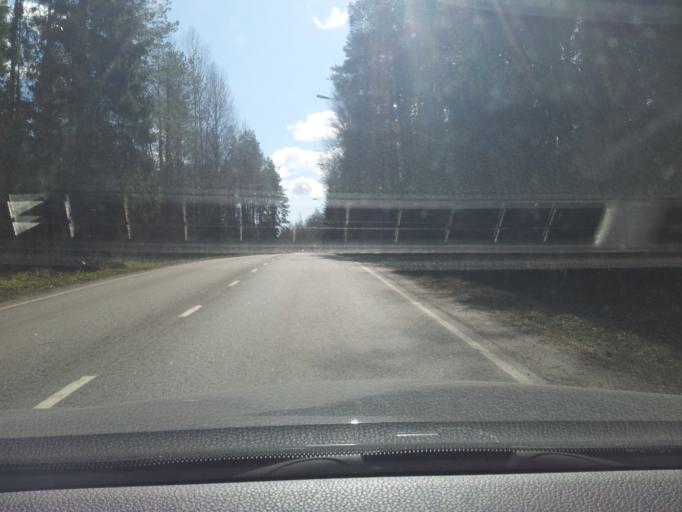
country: FI
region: Uusimaa
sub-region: Helsinki
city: Koukkuniemi
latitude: 60.1497
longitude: 24.7101
